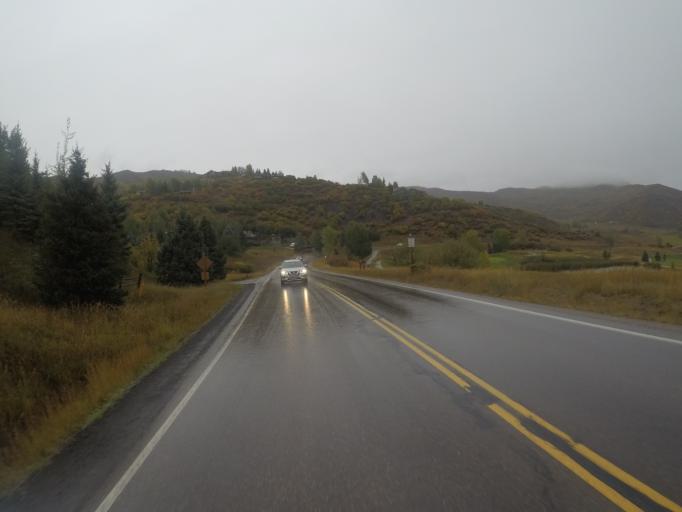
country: US
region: Colorado
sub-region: Pitkin County
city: Snowmass Village
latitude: 39.2199
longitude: -106.9317
